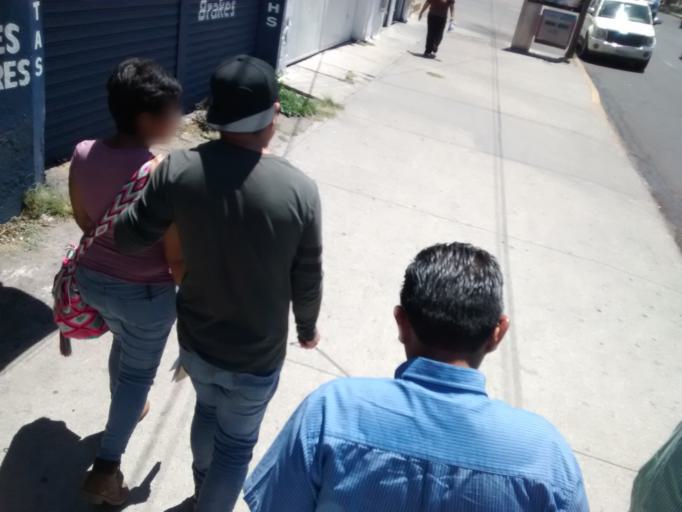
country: MX
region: Puebla
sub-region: San Pedro Cholula
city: Santiago Momoxpan
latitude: 19.0638
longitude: -98.2326
